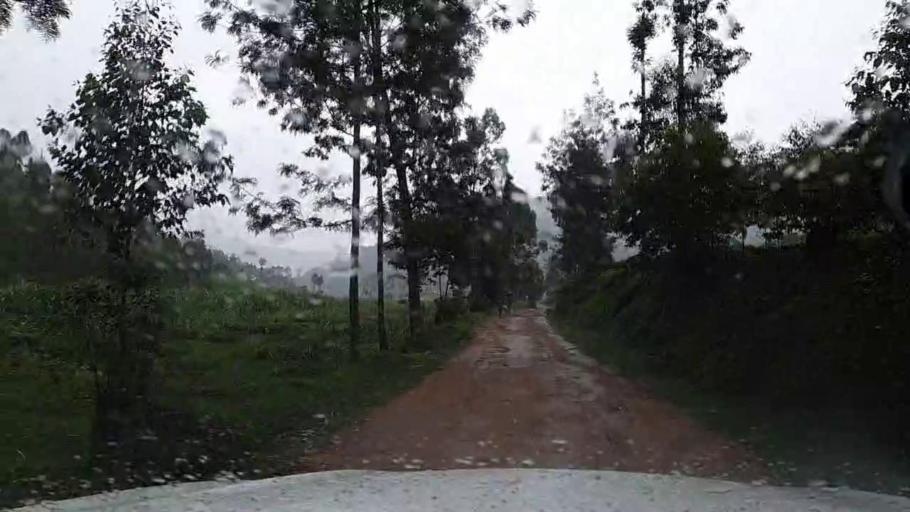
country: RW
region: Northern Province
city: Byumba
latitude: -1.6528
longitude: 29.9233
